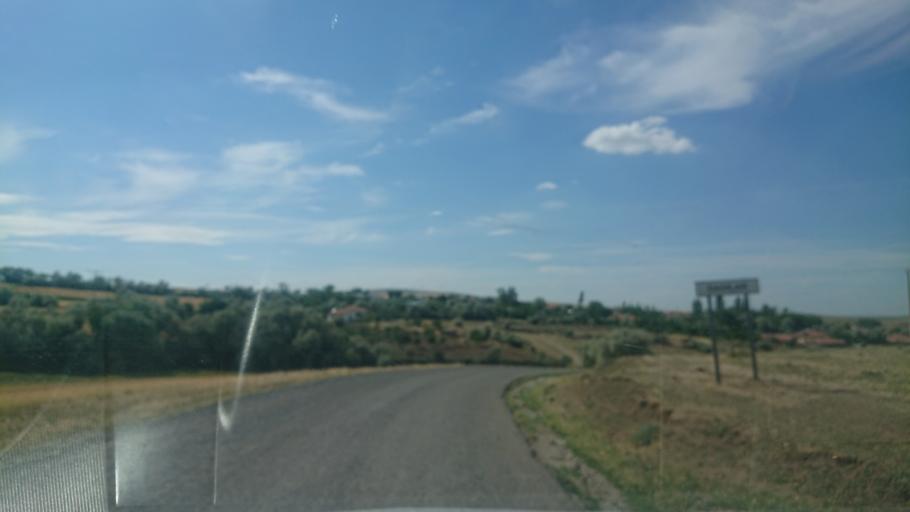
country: TR
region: Aksaray
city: Ortakoy
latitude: 38.8182
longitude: 34.0050
